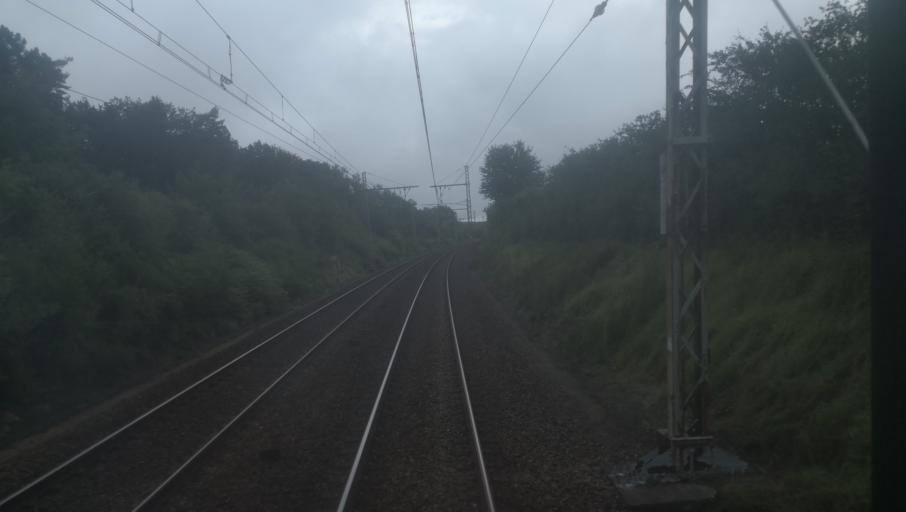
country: FR
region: Centre
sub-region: Departement de l'Indre
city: Luant
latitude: 46.7547
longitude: 1.5973
